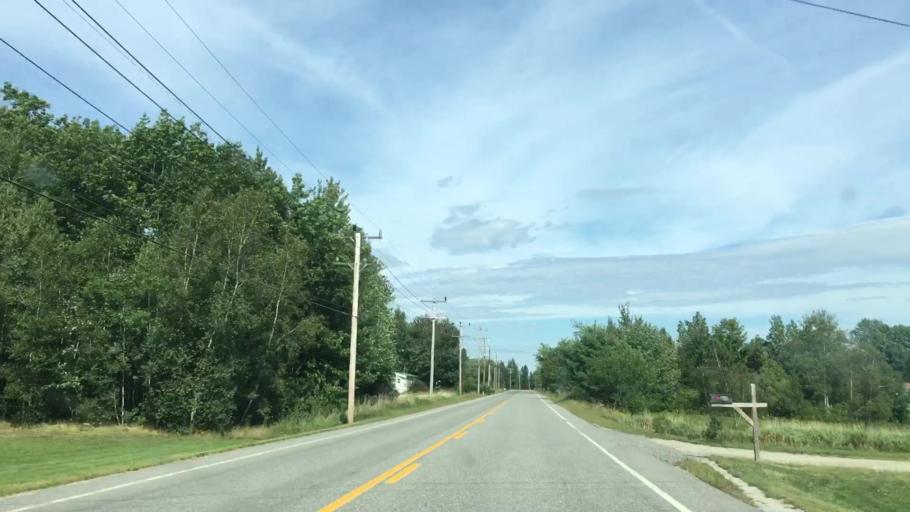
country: US
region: Maine
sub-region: Penobscot County
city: Lincoln
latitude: 45.4243
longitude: -68.4827
